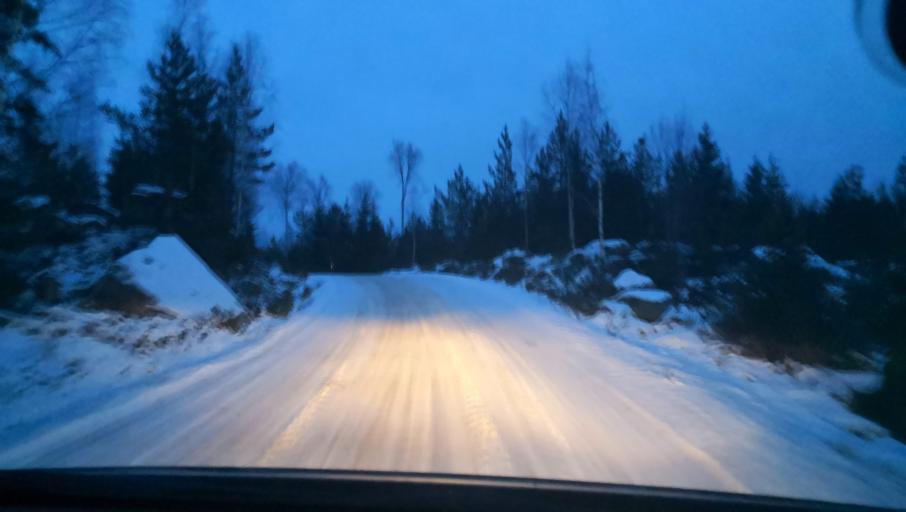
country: SE
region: Dalarna
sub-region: Avesta Kommun
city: Horndal
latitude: 60.2364
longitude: 16.6623
